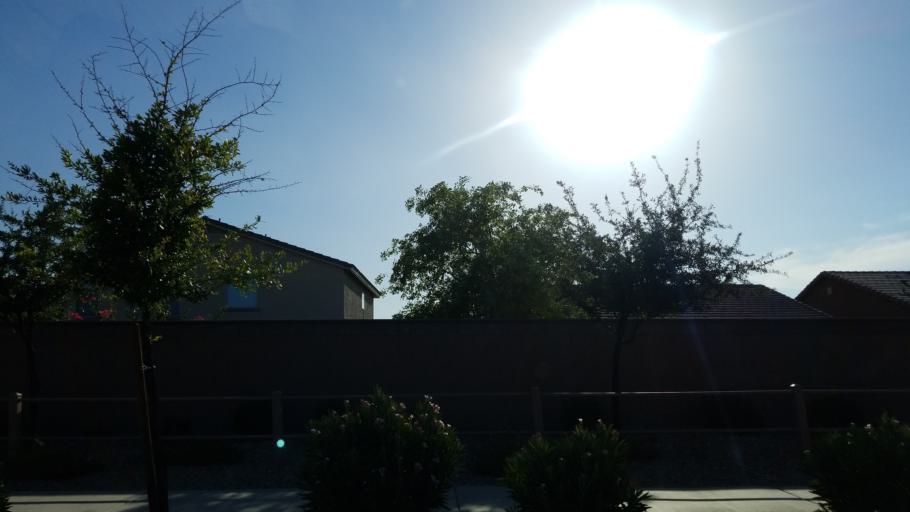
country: US
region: Arizona
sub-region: Maricopa County
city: Laveen
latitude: 33.3841
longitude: -112.2199
